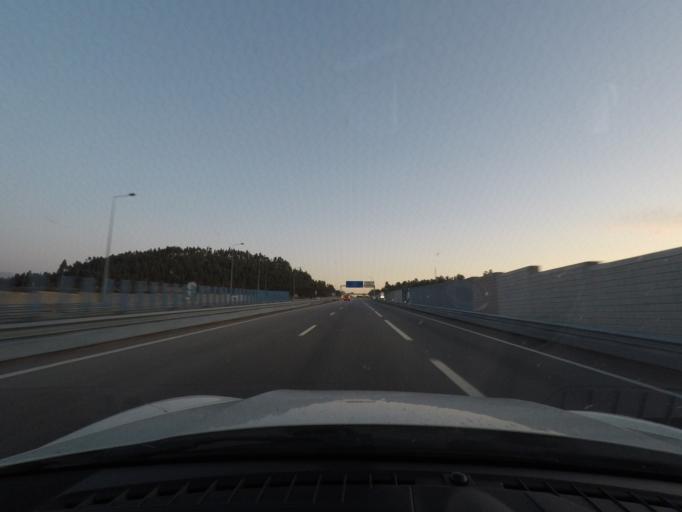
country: PT
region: Porto
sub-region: Pacos de Ferreira
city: Freamunde
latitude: 41.2745
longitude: -8.3280
